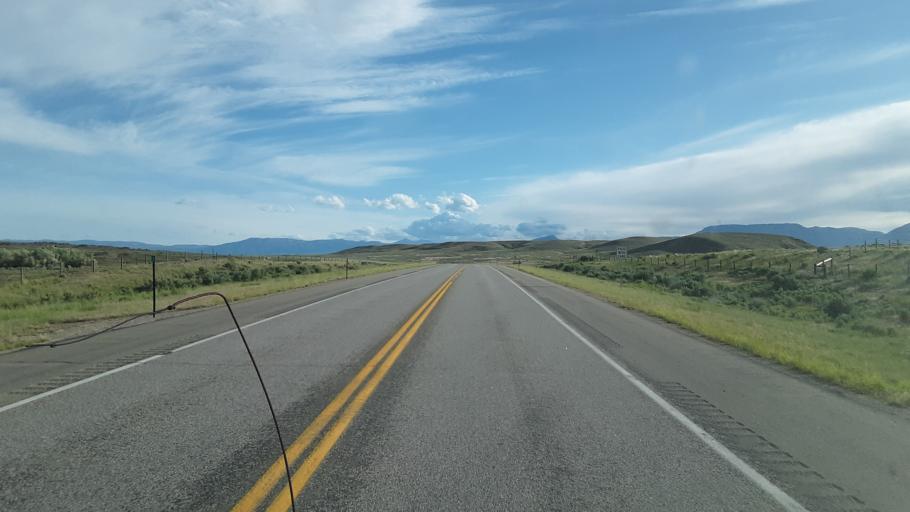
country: US
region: Montana
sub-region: Carbon County
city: Red Lodge
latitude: 44.9576
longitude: -109.0652
